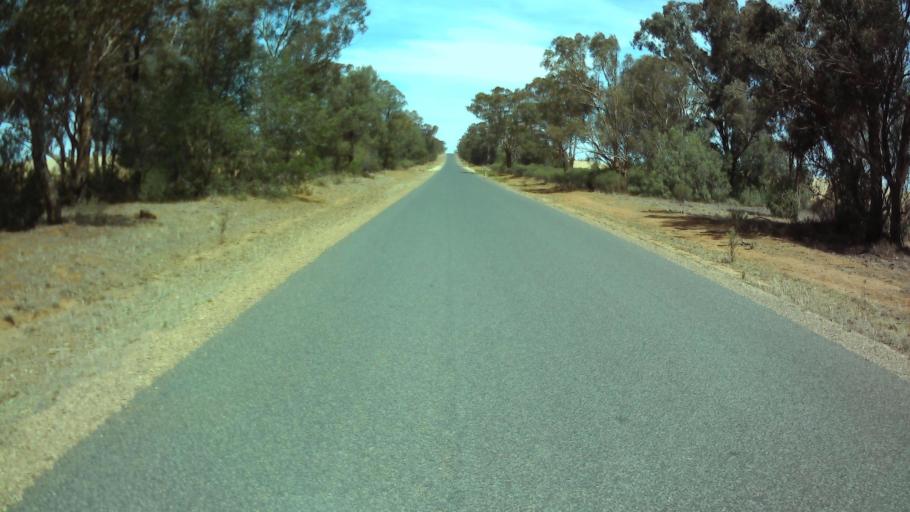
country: AU
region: New South Wales
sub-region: Weddin
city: Grenfell
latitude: -33.8966
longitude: 147.7505
